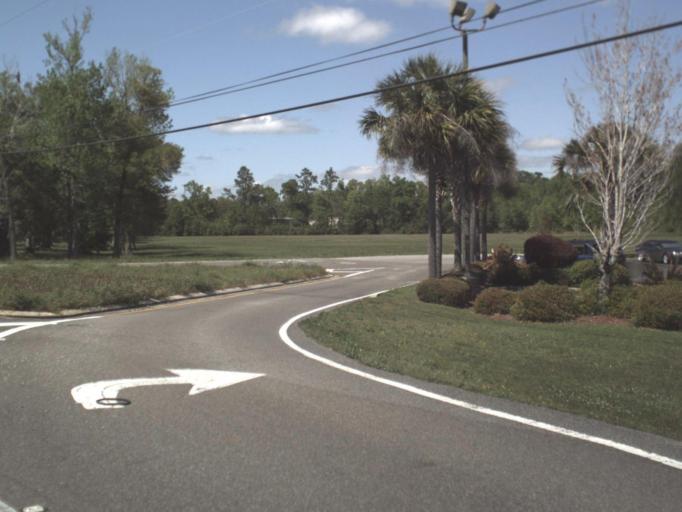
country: US
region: Florida
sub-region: Escambia County
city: Brent
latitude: 30.4859
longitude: -87.2580
